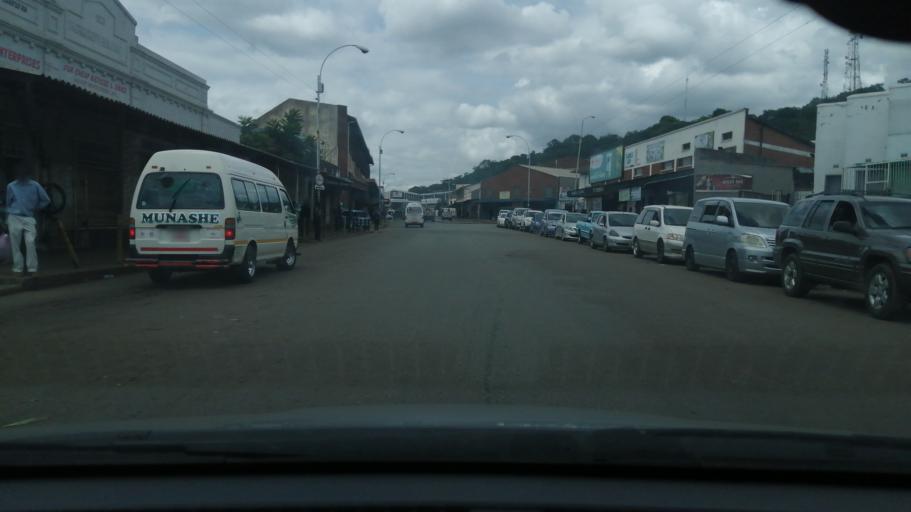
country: ZW
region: Harare
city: Harare
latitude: -17.8398
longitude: 31.0421
